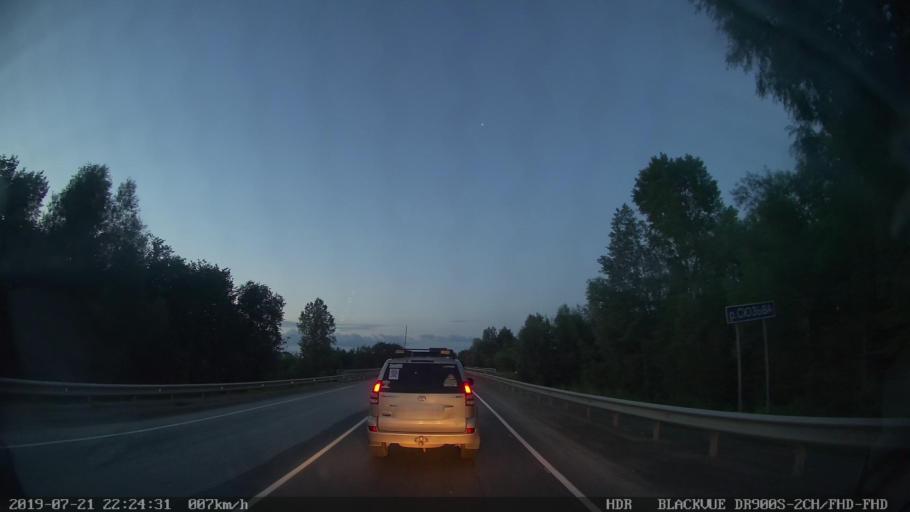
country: RU
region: Perm
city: Chaykovskaya
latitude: 58.0301
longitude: 55.5533
